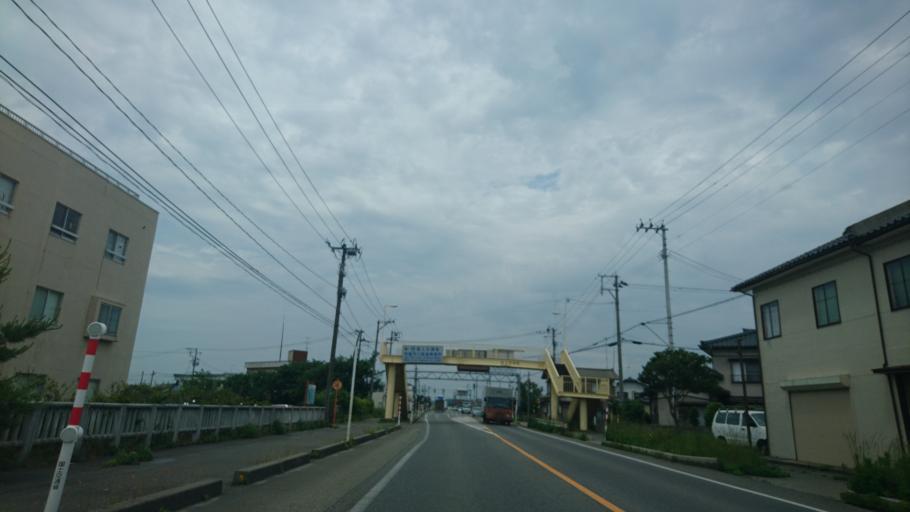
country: JP
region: Niigata
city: Murakami
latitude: 38.1171
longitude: 139.4512
